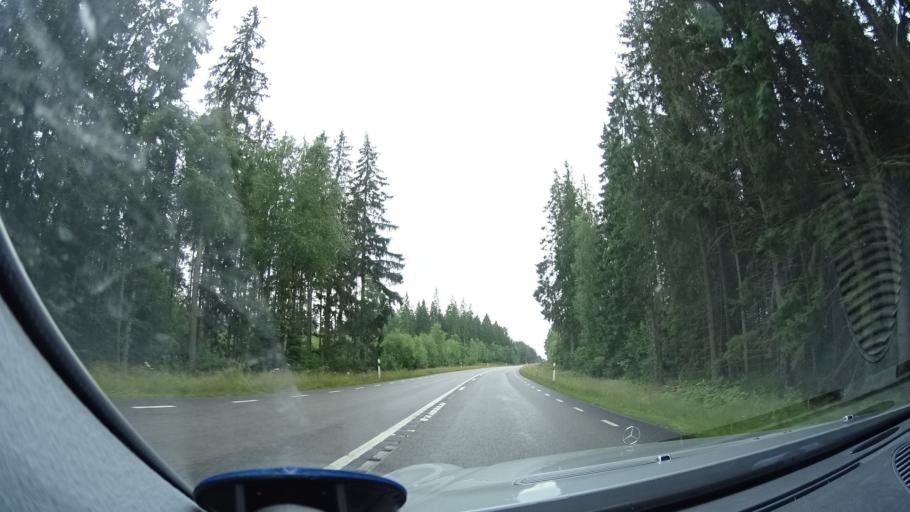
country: SE
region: Kronoberg
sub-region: Tingsryds Kommun
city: Tingsryd
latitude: 56.4612
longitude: 15.0036
